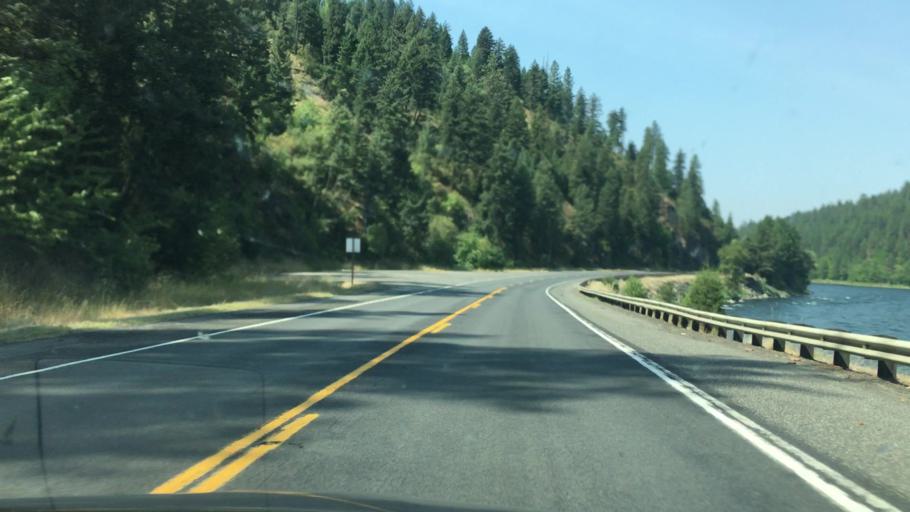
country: US
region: Idaho
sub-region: Clearwater County
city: Orofino
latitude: 46.5020
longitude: -116.3537
